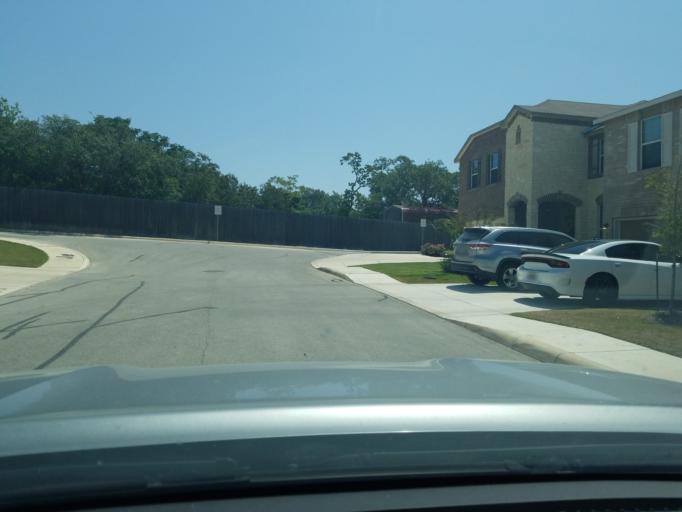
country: US
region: Texas
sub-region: Bexar County
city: Timberwood Park
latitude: 29.7066
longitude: -98.4819
